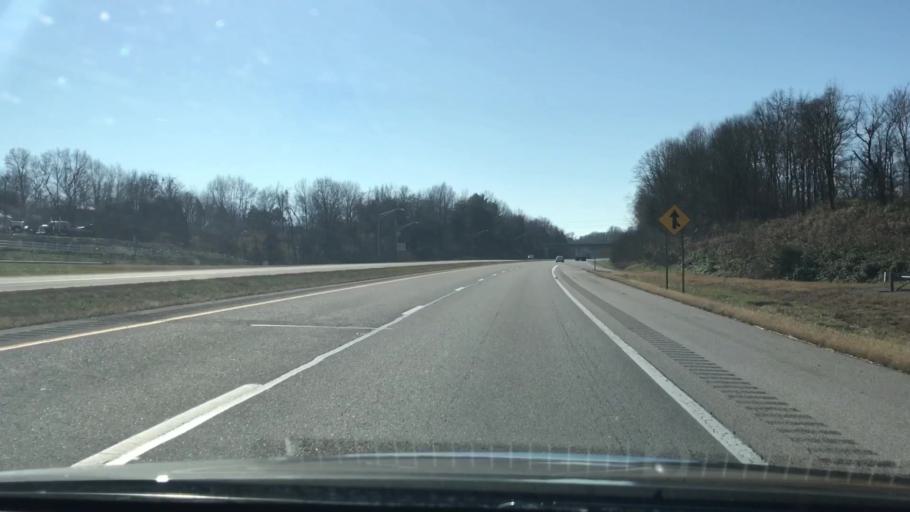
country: US
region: Kentucky
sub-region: Barren County
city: Glasgow
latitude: 36.9833
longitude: -85.8981
